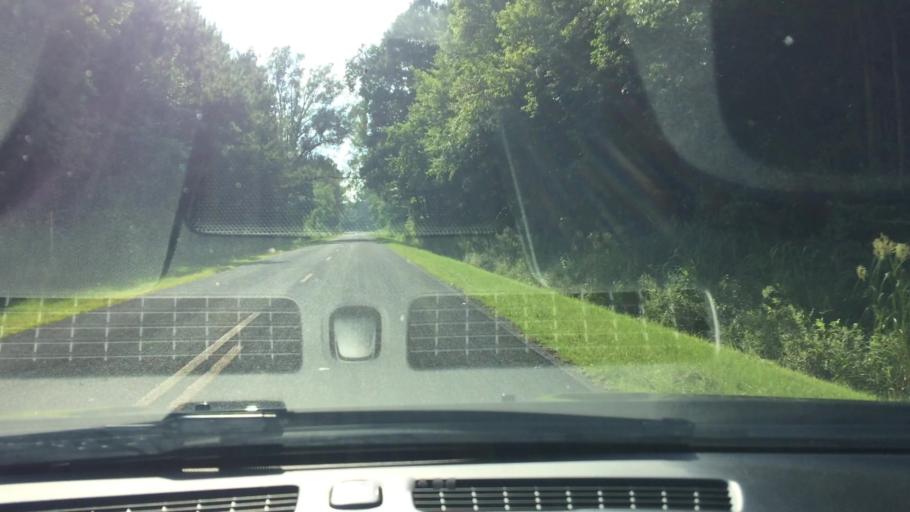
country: US
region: North Carolina
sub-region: Beaufort County
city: River Road
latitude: 35.4579
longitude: -77.0223
